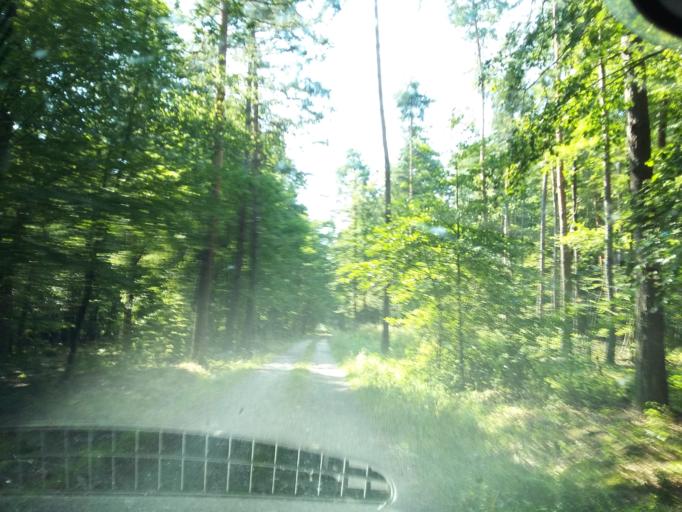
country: SI
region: Hodos-Hodos
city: Hodos
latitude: 46.8522
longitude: 16.3187
